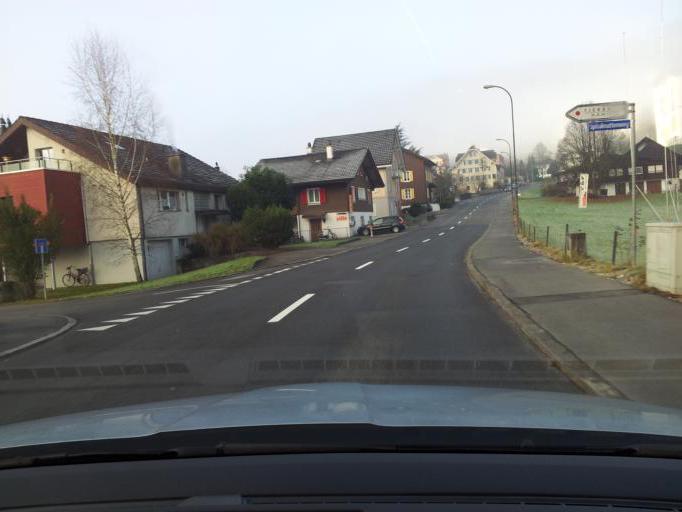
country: CH
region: Obwalden
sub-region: Obwalden
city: Sarnen
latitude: 46.8928
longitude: 8.2416
